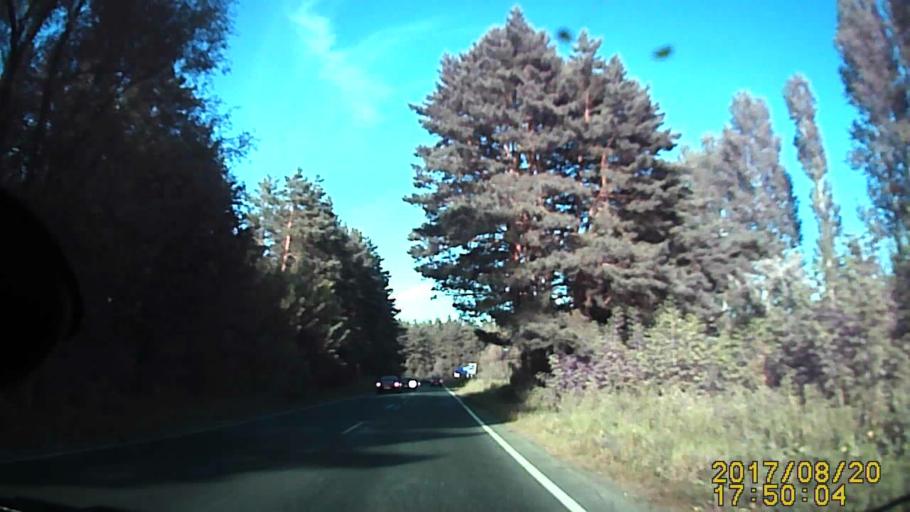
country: RU
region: Ulyanovsk
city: Cherdakly
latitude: 54.4296
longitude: 48.8059
